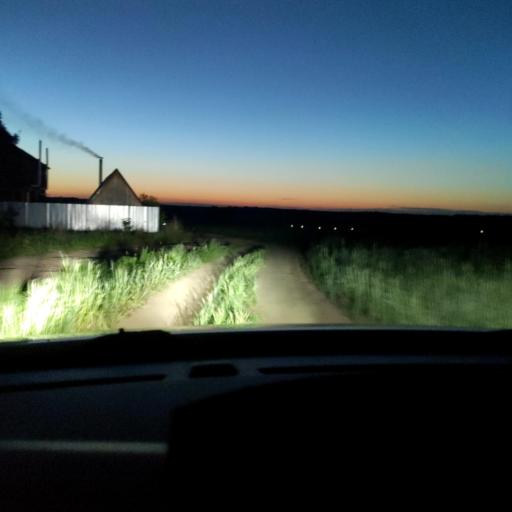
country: RU
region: Tatarstan
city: Vysokaya Gora
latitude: 55.8454
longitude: 49.3328
